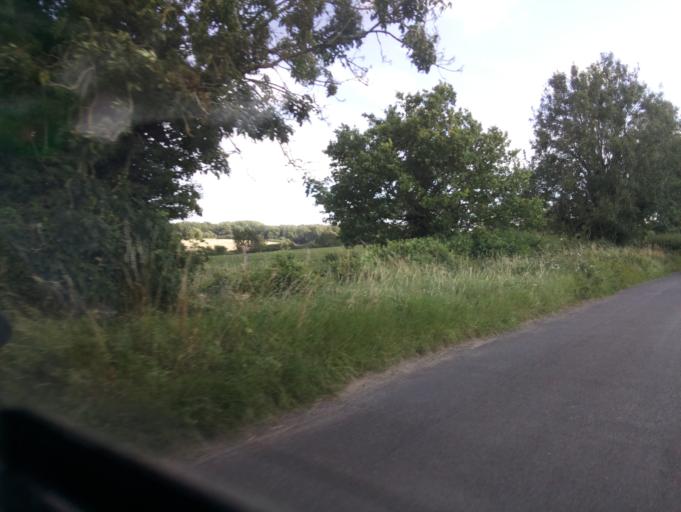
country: GB
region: England
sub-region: Gloucestershire
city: Tetbury
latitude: 51.6538
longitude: -2.1438
